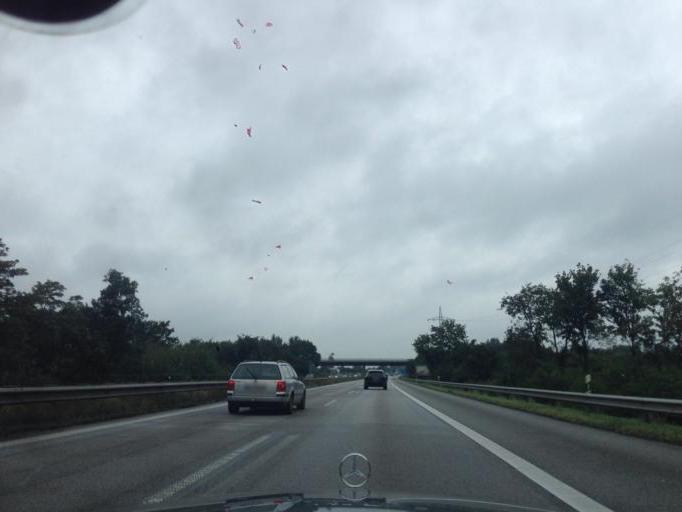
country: DE
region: Schleswig-Holstein
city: Padenstedt
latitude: 54.0527
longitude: 9.9258
